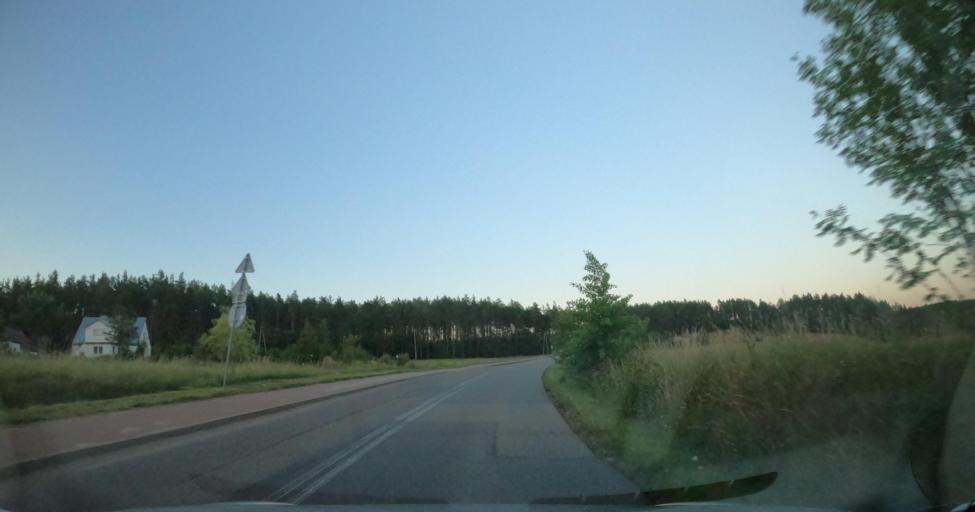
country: PL
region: Pomeranian Voivodeship
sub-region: Powiat wejherowski
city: Linia
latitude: 54.4574
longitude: 18.0076
